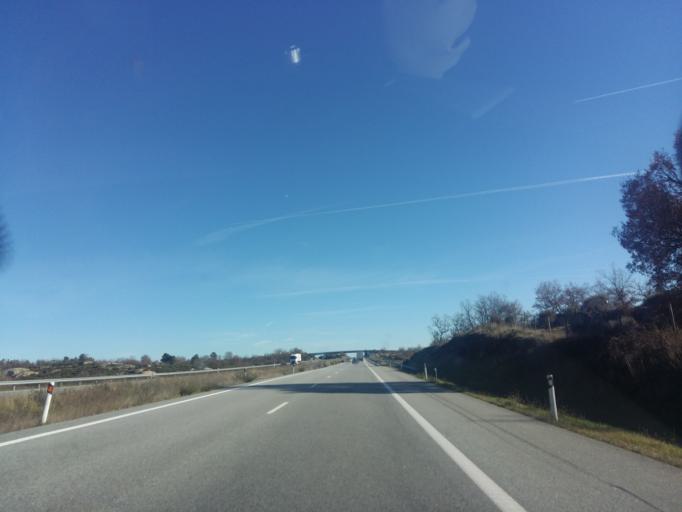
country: PT
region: Guarda
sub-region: Guarda
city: Sequeira
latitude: 40.6025
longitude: -7.1013
